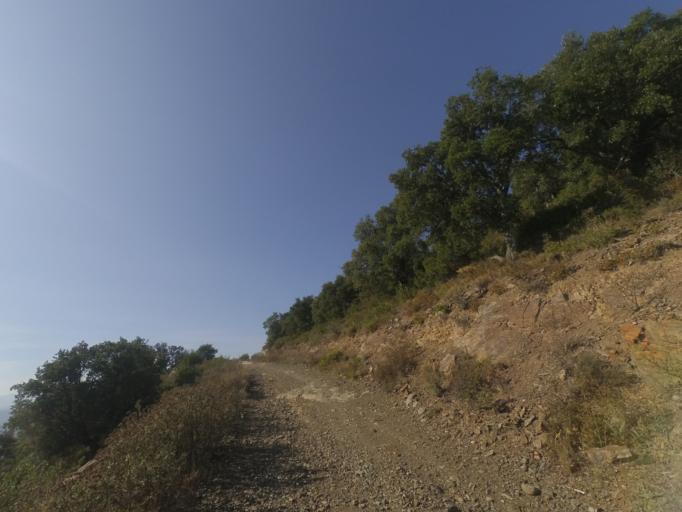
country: FR
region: Languedoc-Roussillon
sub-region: Departement des Pyrenees-Orientales
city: Millas
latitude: 42.7264
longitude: 2.7037
